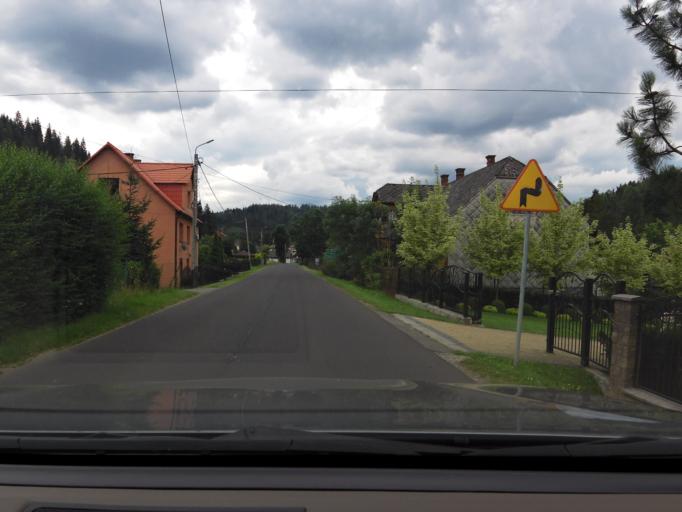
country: PL
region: Silesian Voivodeship
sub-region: Powiat zywiecki
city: Ujsoly
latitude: 49.4715
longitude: 19.1500
